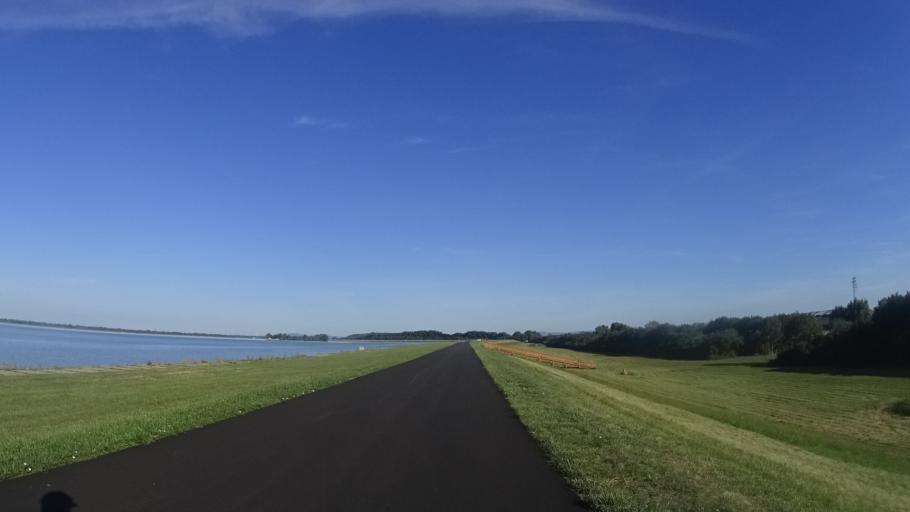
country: SK
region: Trnavsky
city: Samorin
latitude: 48.0143
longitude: 17.2969
